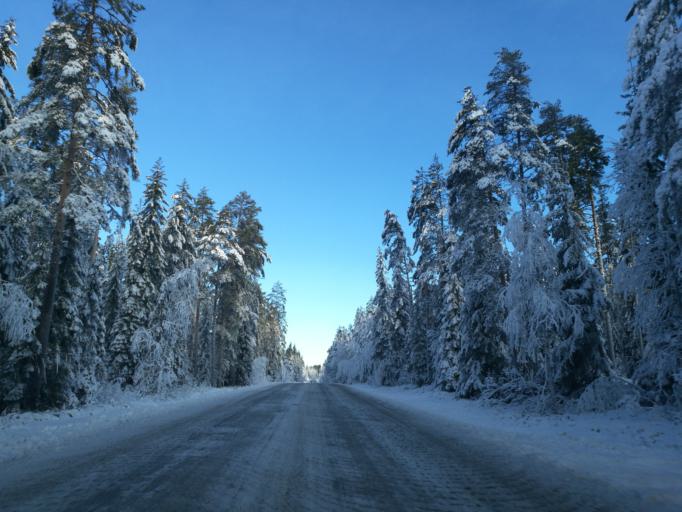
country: NO
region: Hedmark
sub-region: Grue
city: Kirkenaer
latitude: 60.3923
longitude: 12.3667
